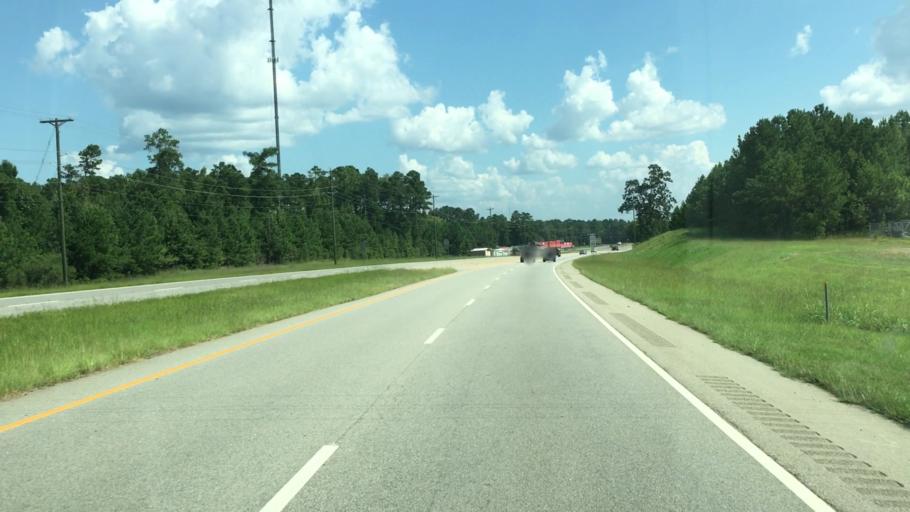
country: US
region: Georgia
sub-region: Baldwin County
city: Milledgeville
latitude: 33.2100
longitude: -83.2992
